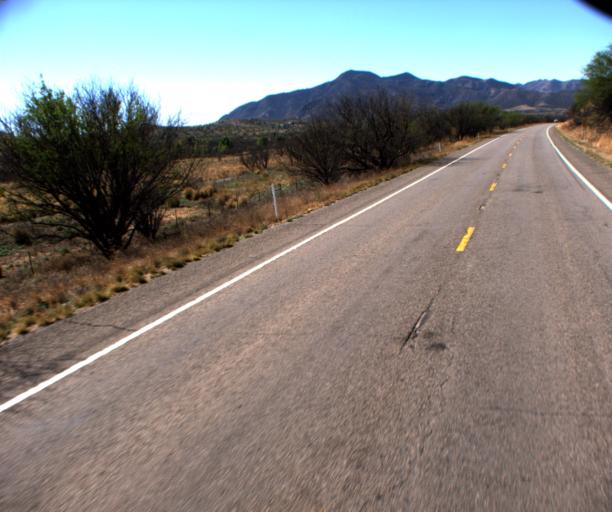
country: US
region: Arizona
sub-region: Santa Cruz County
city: Rio Rico
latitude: 31.5702
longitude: -110.7304
